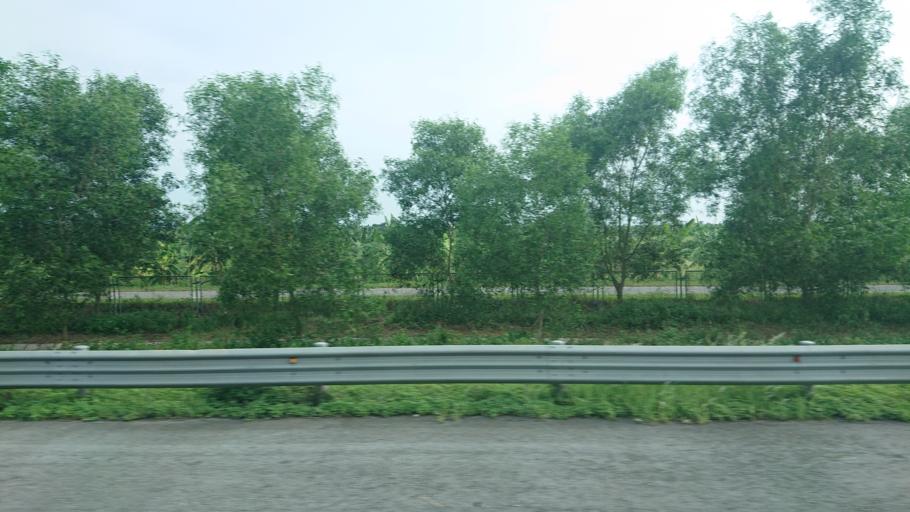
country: VN
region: Hai Phong
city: An Lao
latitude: 20.8169
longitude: 106.4881
